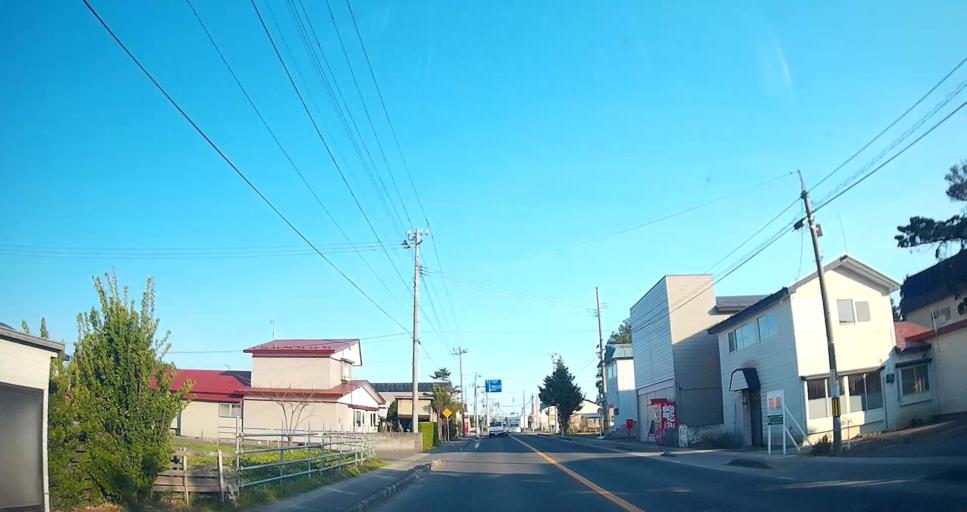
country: JP
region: Aomori
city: Mutsu
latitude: 41.2733
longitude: 141.2160
